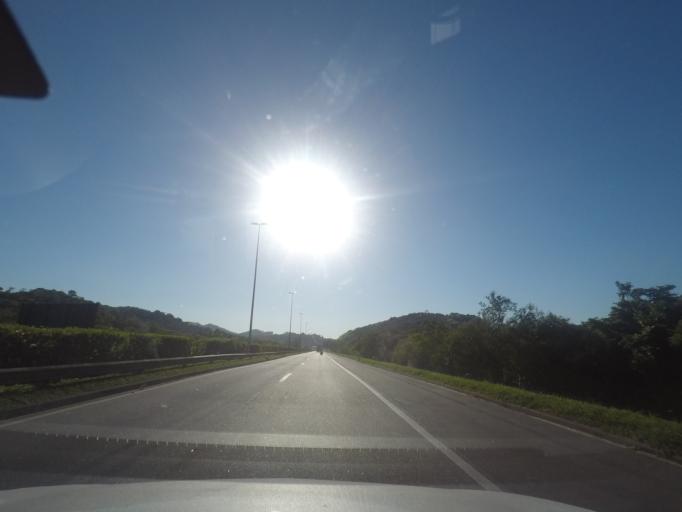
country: BR
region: Rio de Janeiro
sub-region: Petropolis
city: Petropolis
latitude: -22.6546
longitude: -43.1427
